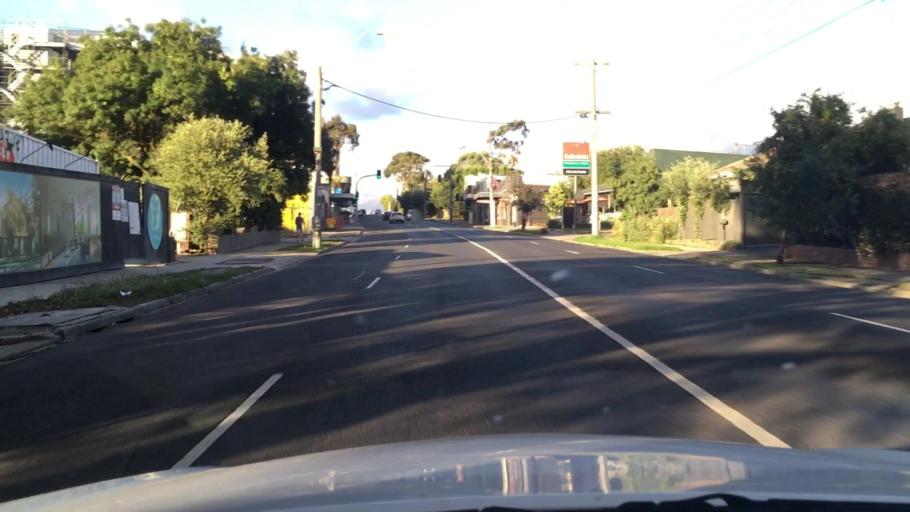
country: AU
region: Victoria
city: Alphington
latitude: -37.7761
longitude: 145.0386
